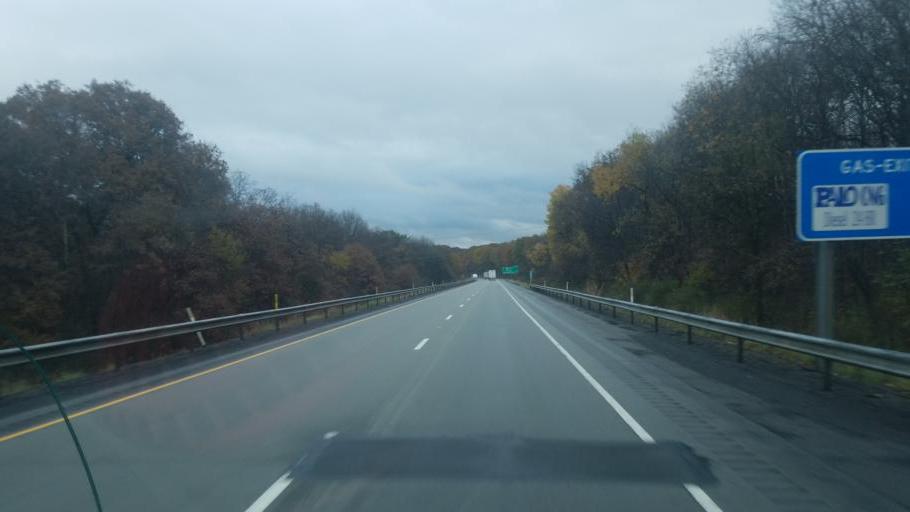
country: US
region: Pennsylvania
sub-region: Clarion County
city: Clarion
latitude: 41.1767
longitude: -79.3587
